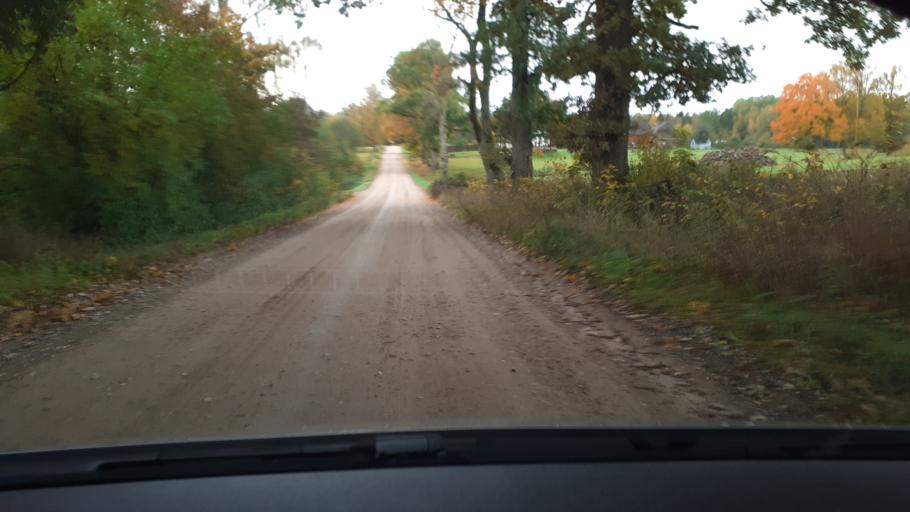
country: LV
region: Kuldigas Rajons
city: Kuldiga
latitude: 57.0285
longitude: 21.9152
